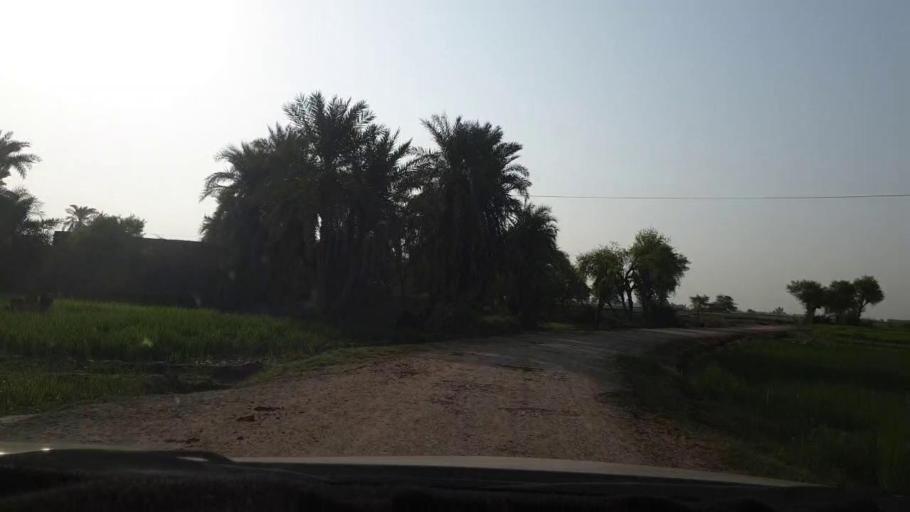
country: PK
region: Sindh
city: Larkana
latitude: 27.5116
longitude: 68.1813
